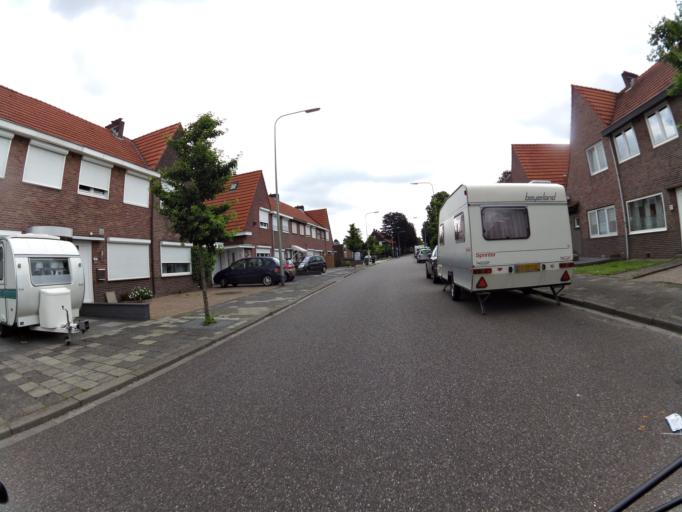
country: NL
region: Limburg
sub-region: Gemeente Kerkrade
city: Kerkrade
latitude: 50.9131
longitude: 6.0434
